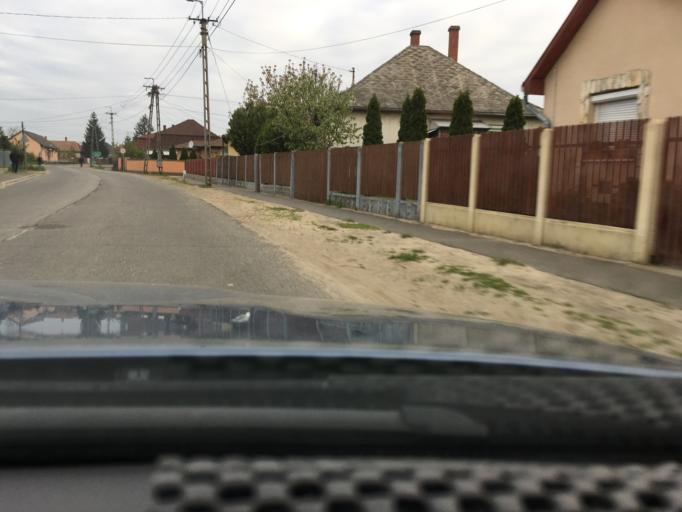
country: HU
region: Hajdu-Bihar
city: Hajdusamson
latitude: 47.5976
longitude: 21.7616
